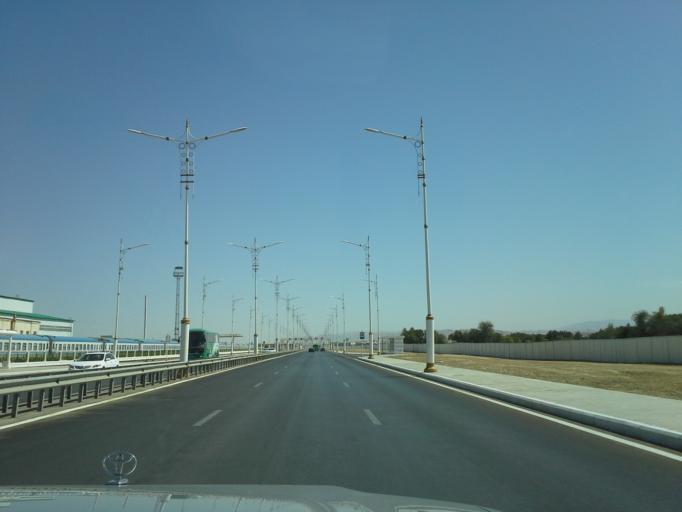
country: TM
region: Ahal
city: Ashgabat
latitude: 37.9355
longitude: 58.4101
